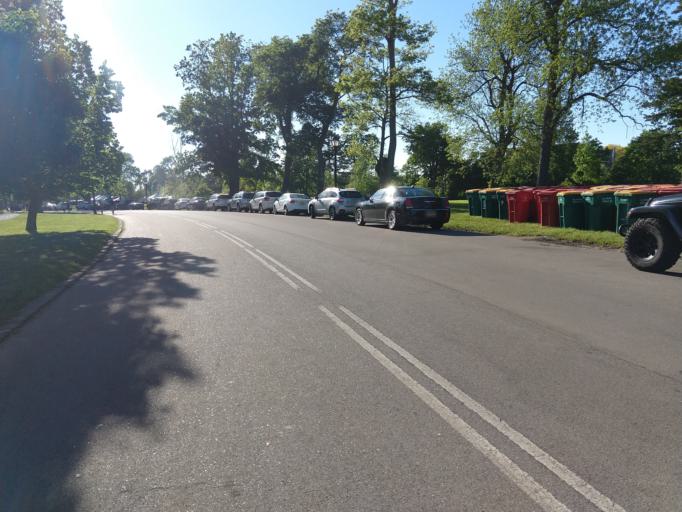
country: US
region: New York
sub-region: Erie County
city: Kenmore
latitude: 42.9398
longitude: -78.8567
